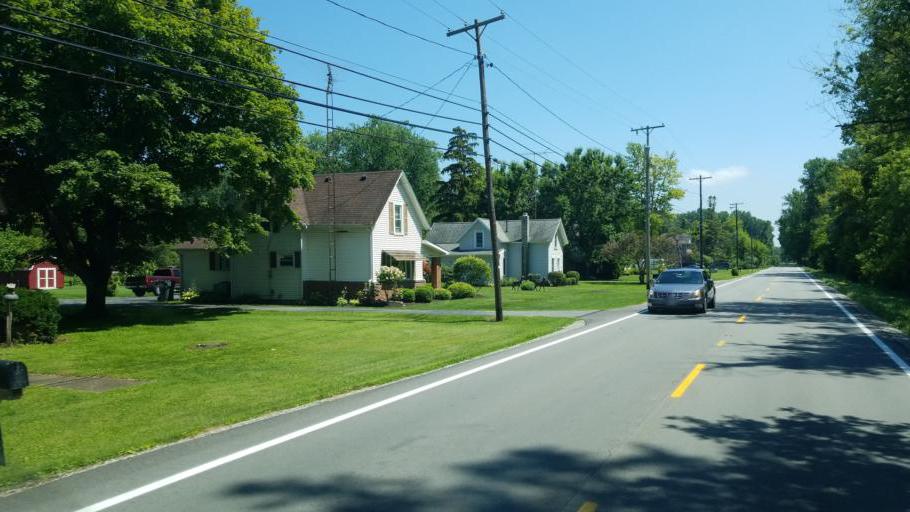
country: US
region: Ohio
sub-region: Erie County
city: Sandusky
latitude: 41.4139
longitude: -82.8151
